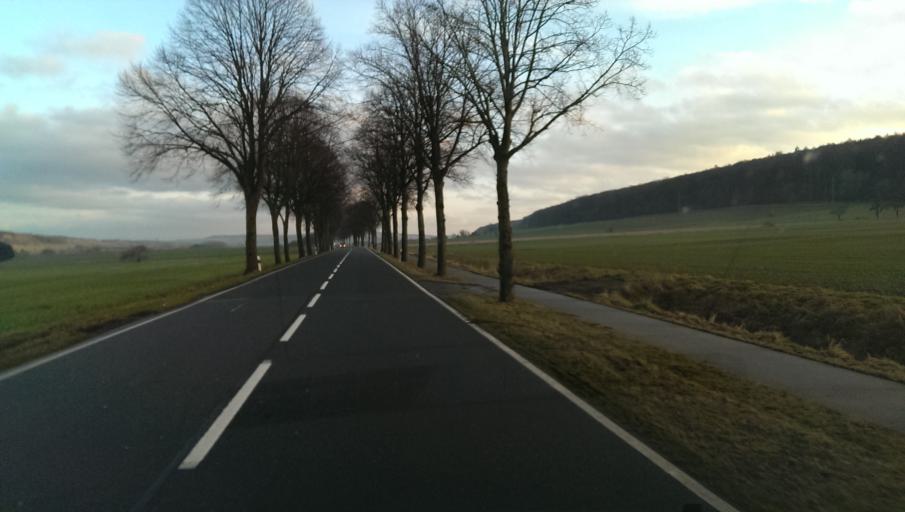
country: DE
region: Lower Saxony
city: Eimen
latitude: 51.8848
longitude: 9.7566
